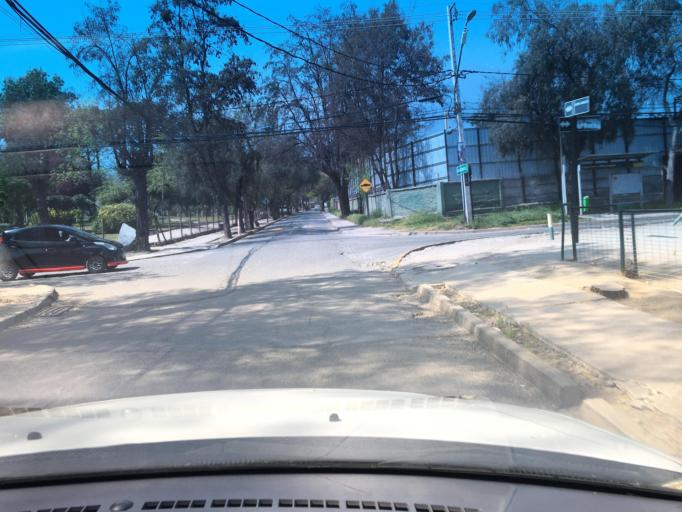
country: CL
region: Santiago Metropolitan
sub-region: Provincia de Santiago
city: Villa Presidente Frei, Nunoa, Santiago, Chile
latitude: -33.5144
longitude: -70.5482
